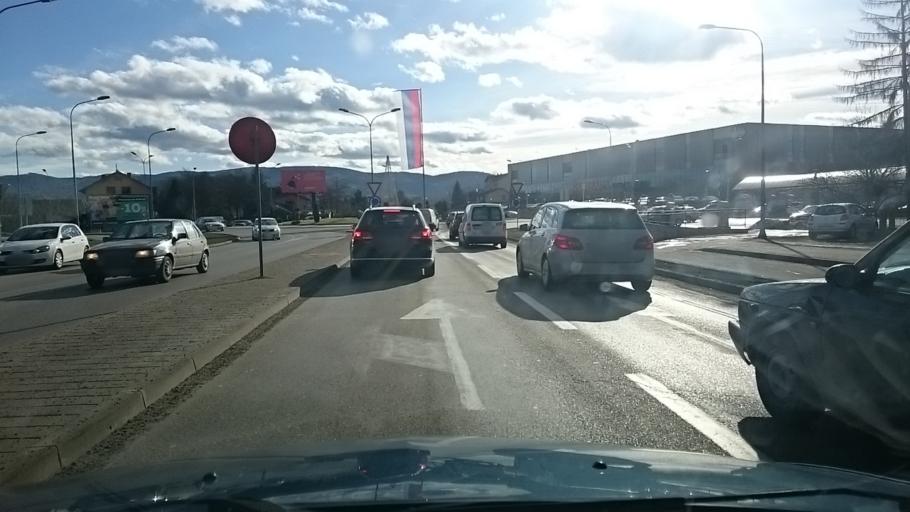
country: BA
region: Republika Srpska
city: Banja Luka
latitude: 44.7915
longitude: 17.1992
